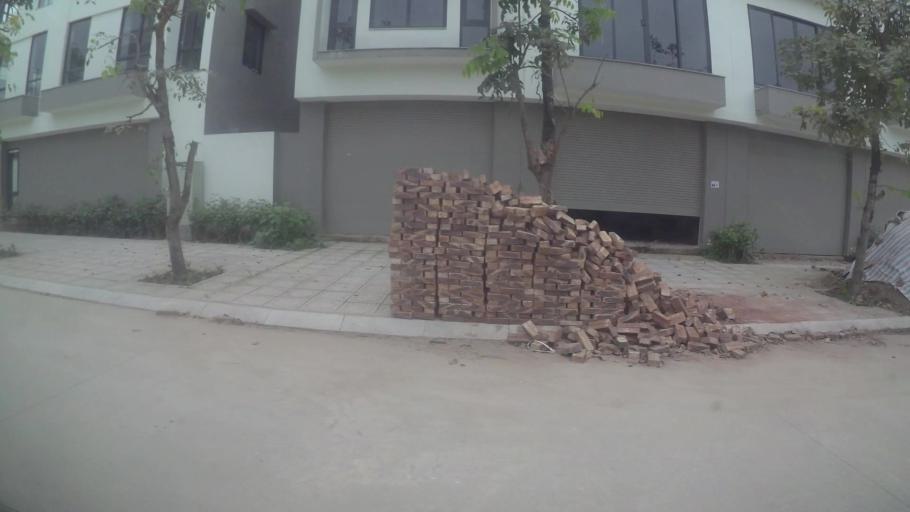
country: VN
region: Ha Noi
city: Ha Dong
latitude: 20.9880
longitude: 105.7428
